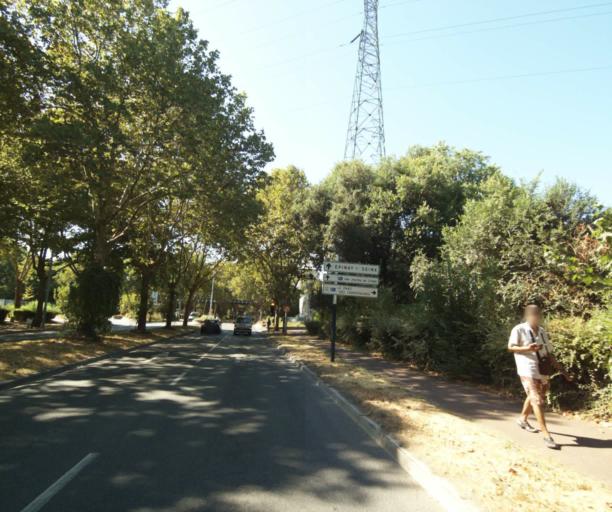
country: FR
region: Ile-de-France
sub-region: Departement des Hauts-de-Seine
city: Villeneuve-la-Garenne
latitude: 48.9408
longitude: 2.3230
